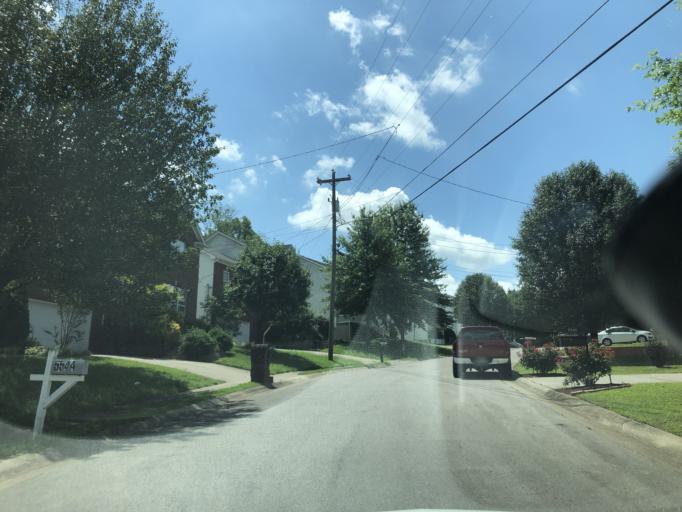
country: US
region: Tennessee
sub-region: Rutherford County
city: La Vergne
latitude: 36.0379
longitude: -86.6245
